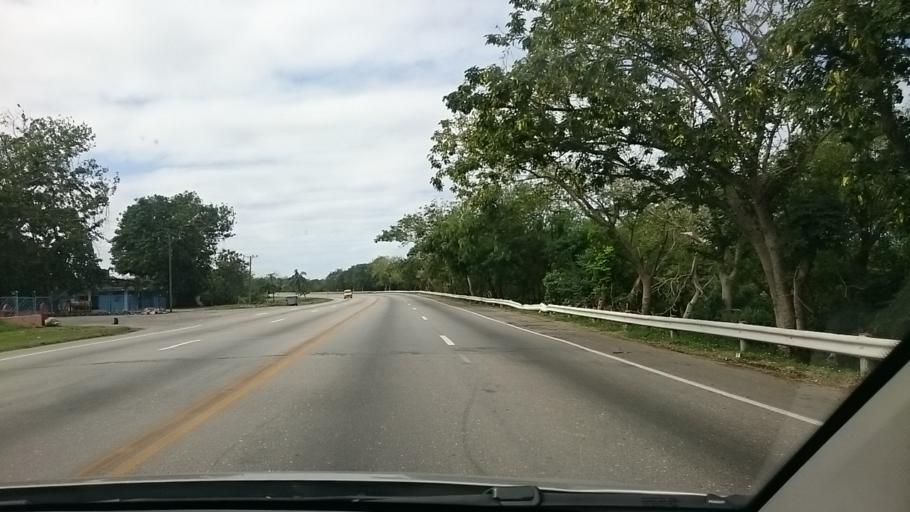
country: CU
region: La Habana
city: Alamar
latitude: 23.1684
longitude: -82.2545
